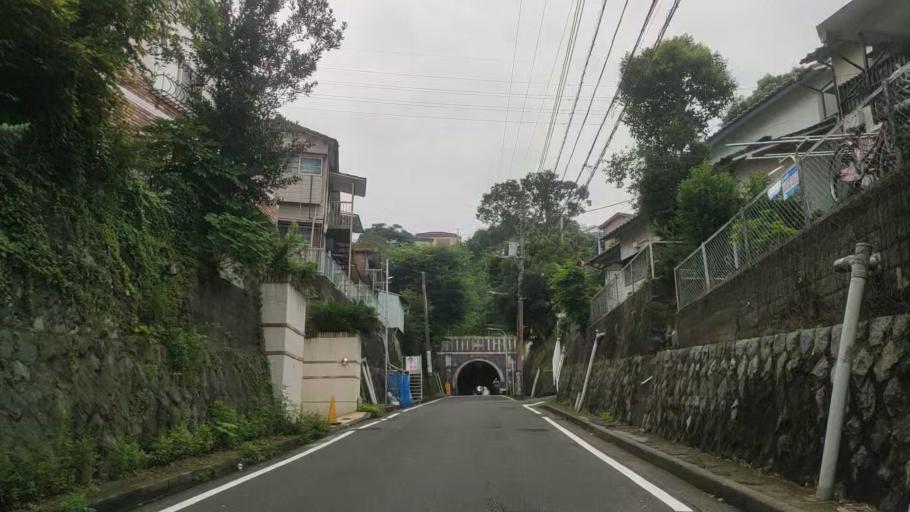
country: JP
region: Kanagawa
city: Yokohama
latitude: 35.4457
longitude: 139.6016
